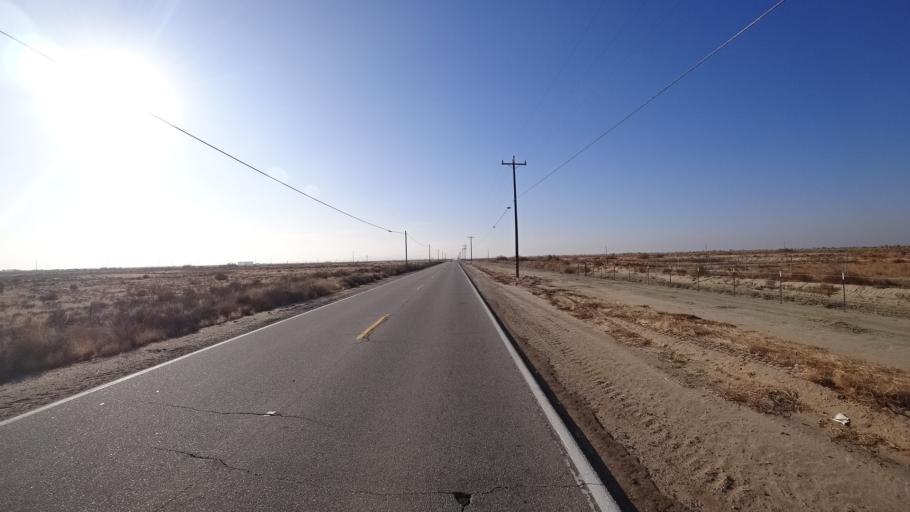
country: US
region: California
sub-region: Kern County
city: Rosedale
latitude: 35.2961
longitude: -119.1951
